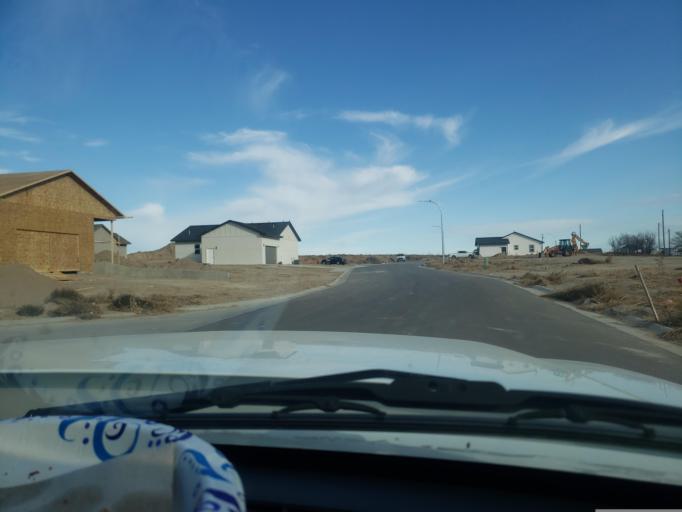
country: US
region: Kansas
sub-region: Finney County
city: Garden City
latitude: 37.9825
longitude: -100.8263
